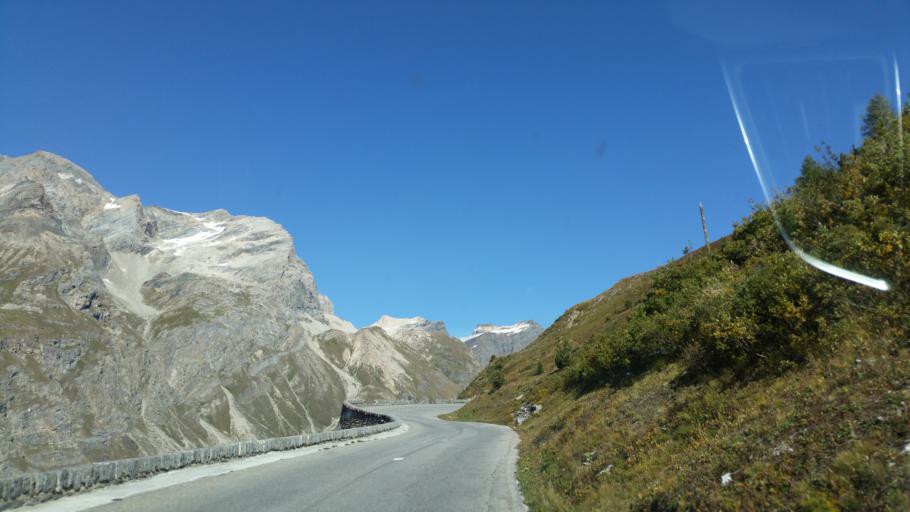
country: FR
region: Rhone-Alpes
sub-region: Departement de la Savoie
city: Val-d'Isere
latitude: 45.4465
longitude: 7.0233
